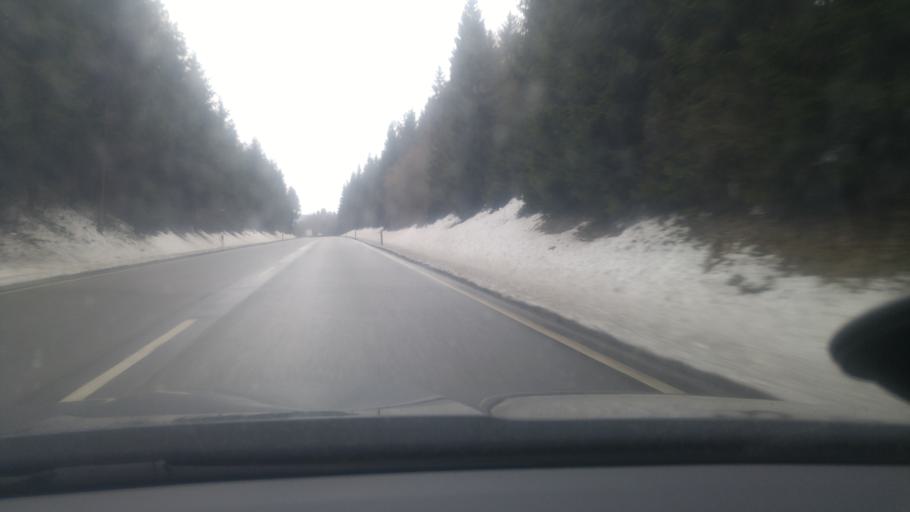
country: DE
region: Baden-Wuerttemberg
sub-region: Freiburg Region
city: Dauchingen
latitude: 48.0738
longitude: 8.5862
